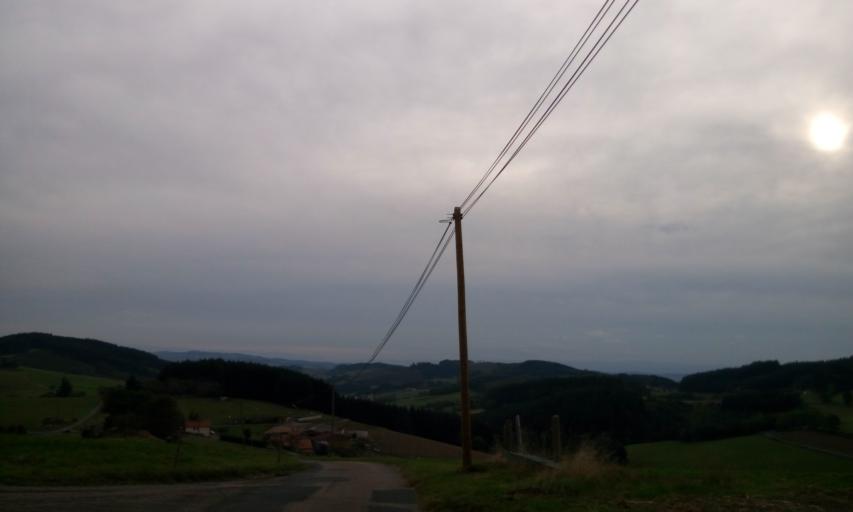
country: FR
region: Rhone-Alpes
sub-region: Departement du Rhone
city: Cublize
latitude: 46.0749
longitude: 4.3692
